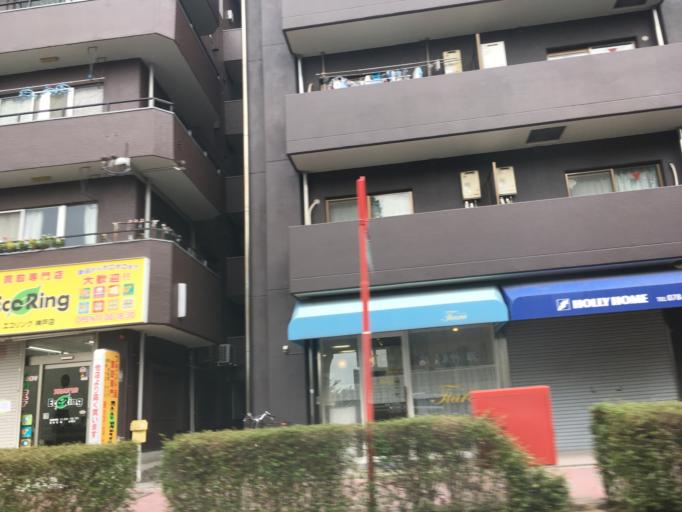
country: JP
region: Hyogo
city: Kobe
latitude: 34.7106
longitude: 135.2205
